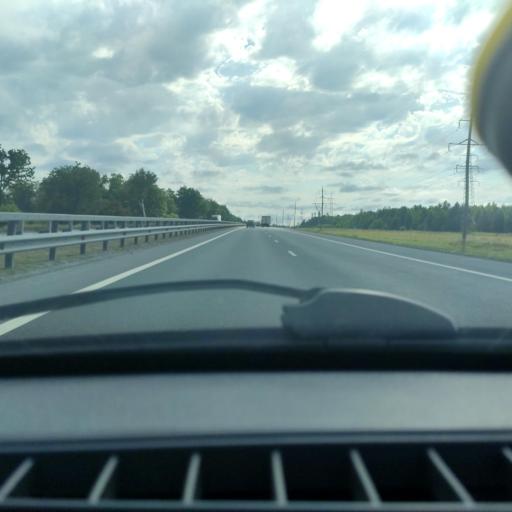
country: RU
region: Samara
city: Pribrezhnyy
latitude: 53.5172
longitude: 49.7951
